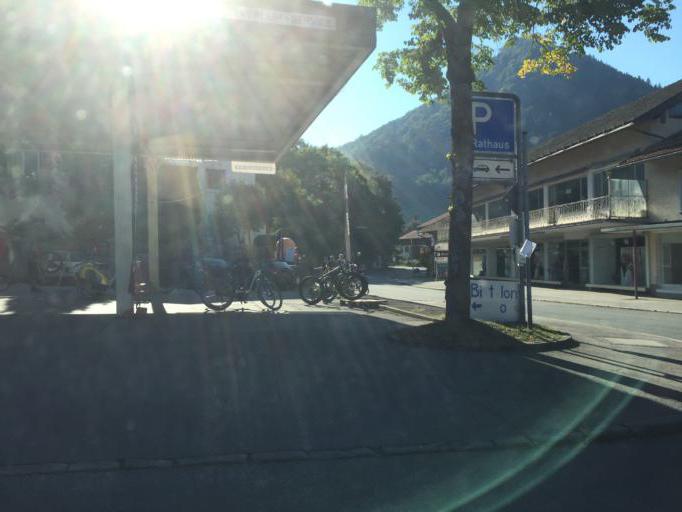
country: DE
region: Bavaria
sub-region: Upper Bavaria
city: Ruhpolding
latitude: 47.7640
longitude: 12.6442
